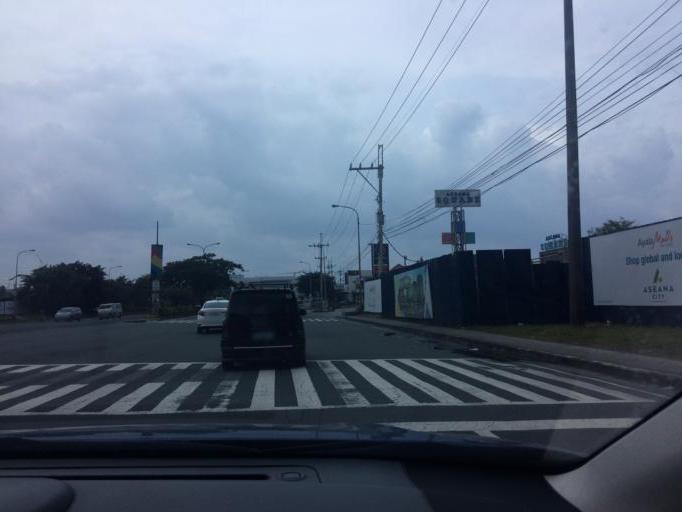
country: PH
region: Metro Manila
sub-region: Makati City
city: Makati City
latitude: 14.5224
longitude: 120.9905
